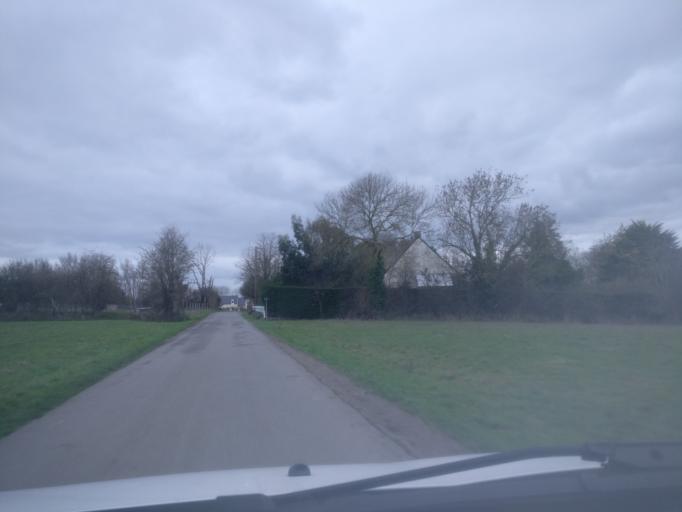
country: FR
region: Lower Normandy
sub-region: Departement de la Manche
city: Marcey-les-Greves
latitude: 48.6630
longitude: -1.4370
